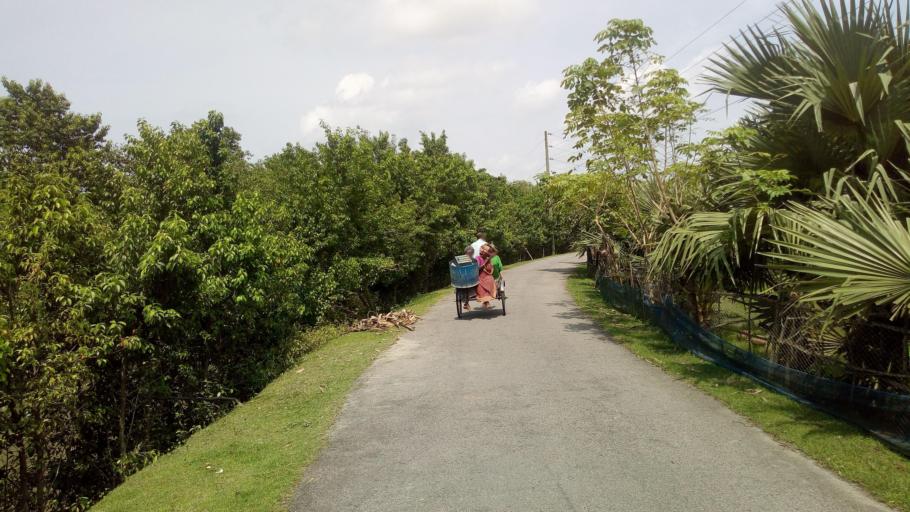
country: BD
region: Khulna
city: Phultala
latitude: 22.5808
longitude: 89.4528
